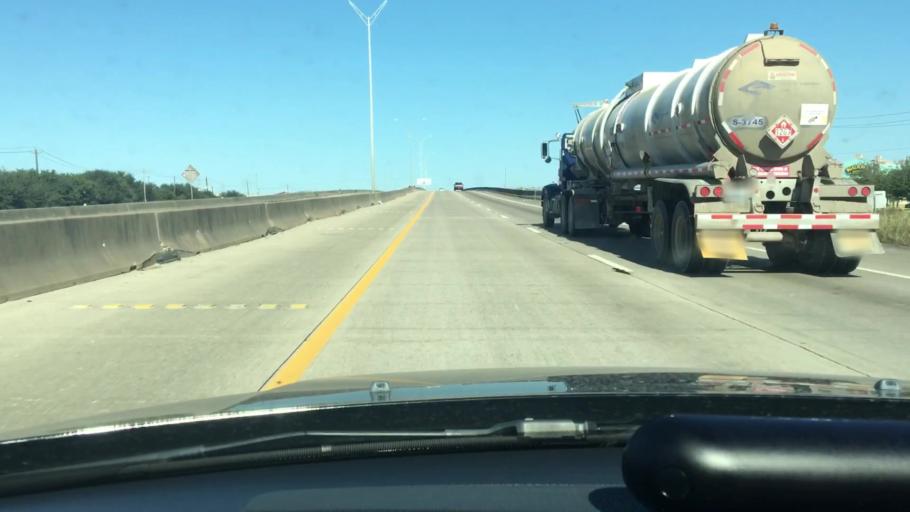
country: US
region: Texas
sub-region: Harris County
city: Cloverleaf
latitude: 29.8055
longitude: -95.1633
